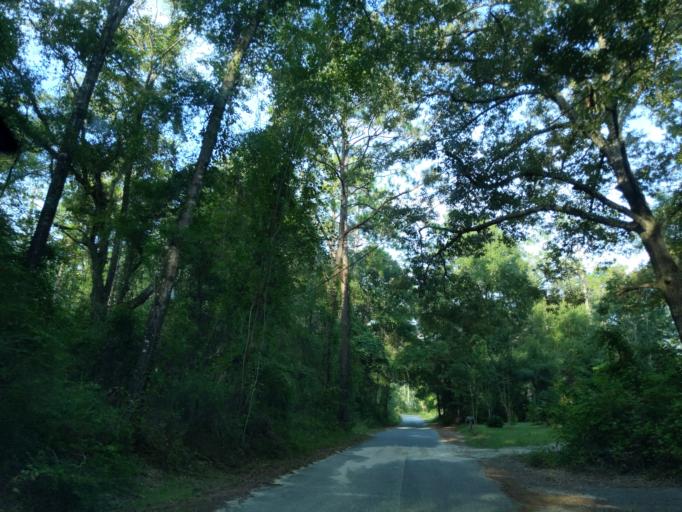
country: US
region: Florida
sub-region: Leon County
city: Tallahassee
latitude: 30.3508
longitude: -84.3630
